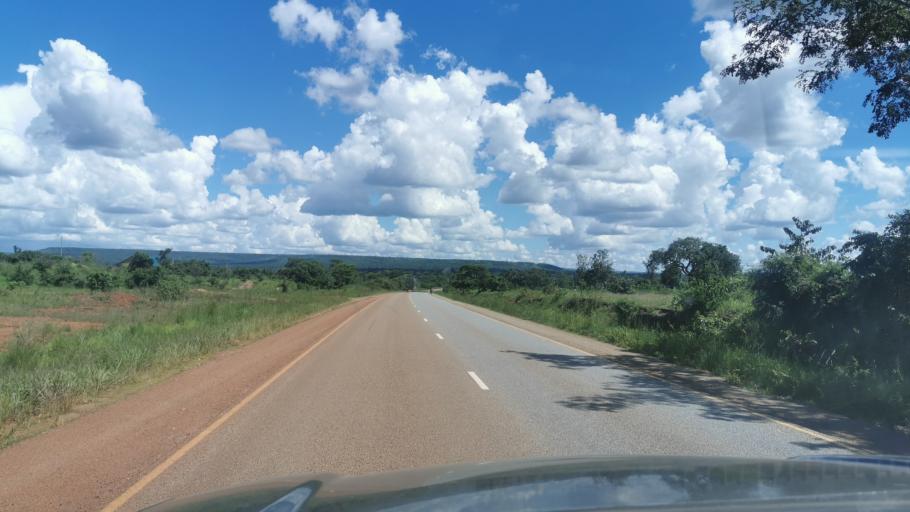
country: TZ
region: Kigoma
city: Kakonko
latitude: -3.0438
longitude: 31.2447
